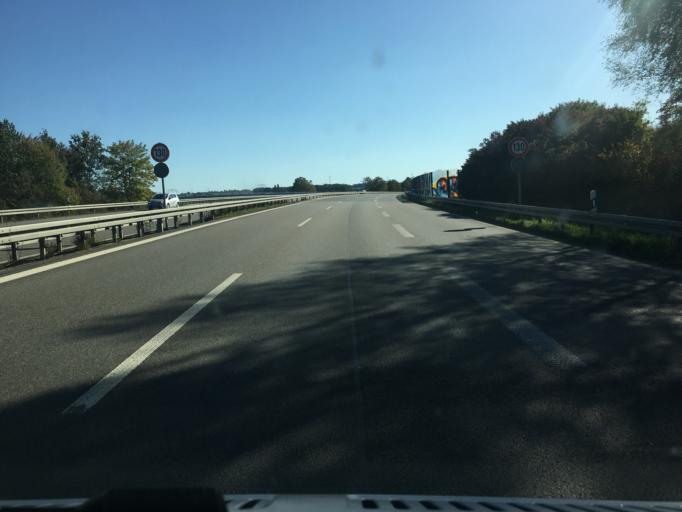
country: DE
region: Saxony
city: Dennheritz
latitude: 50.7843
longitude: 12.4899
